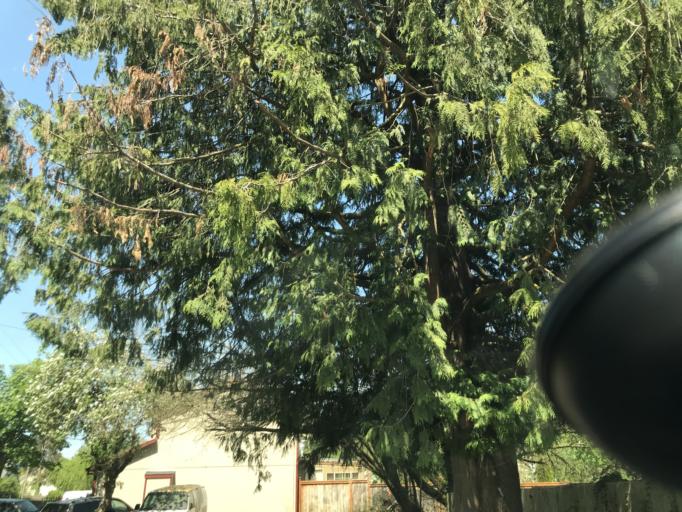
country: US
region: Oregon
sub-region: Multnomah County
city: Lents
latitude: 45.4932
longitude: -122.5598
